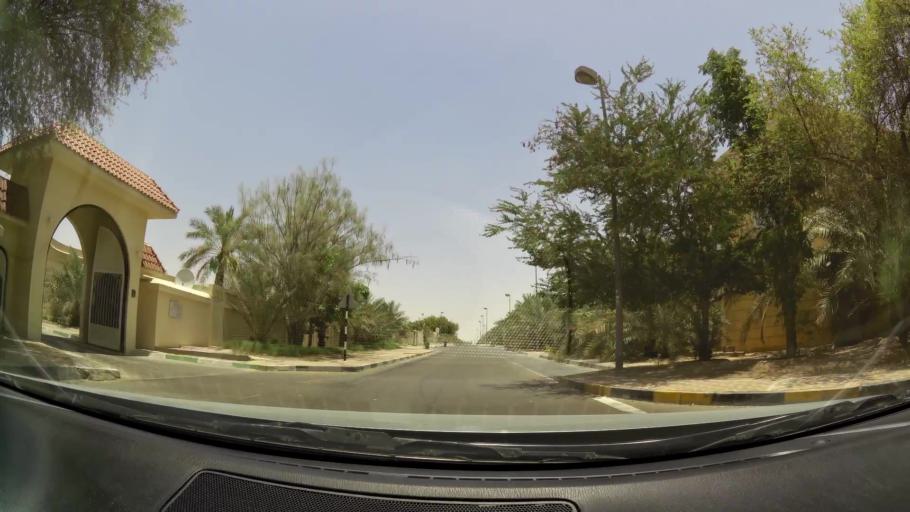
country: OM
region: Al Buraimi
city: Al Buraymi
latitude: 24.2654
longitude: 55.7261
